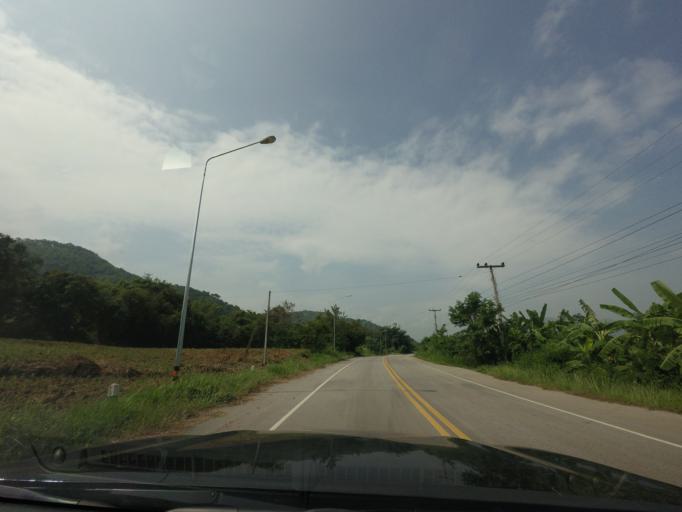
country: LA
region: Xiagnabouli
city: Muang Kenthao
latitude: 17.6808
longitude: 101.3809
